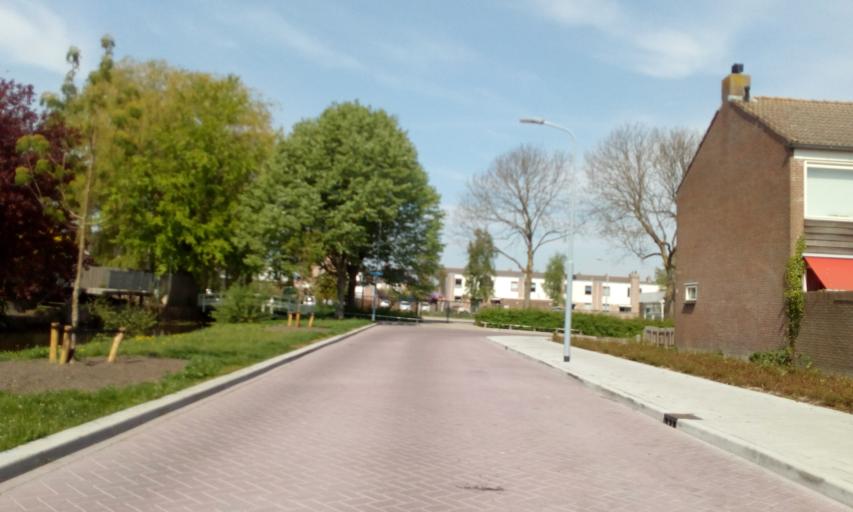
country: NL
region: South Holland
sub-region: Gemeente Lisse
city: Lisse
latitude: 52.2580
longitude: 4.5729
